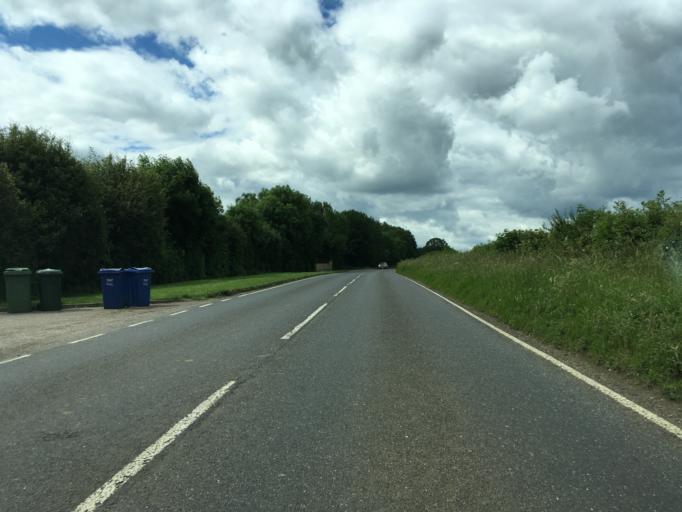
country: GB
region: England
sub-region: Oxfordshire
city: Bloxham
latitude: 52.0080
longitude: -1.3882
